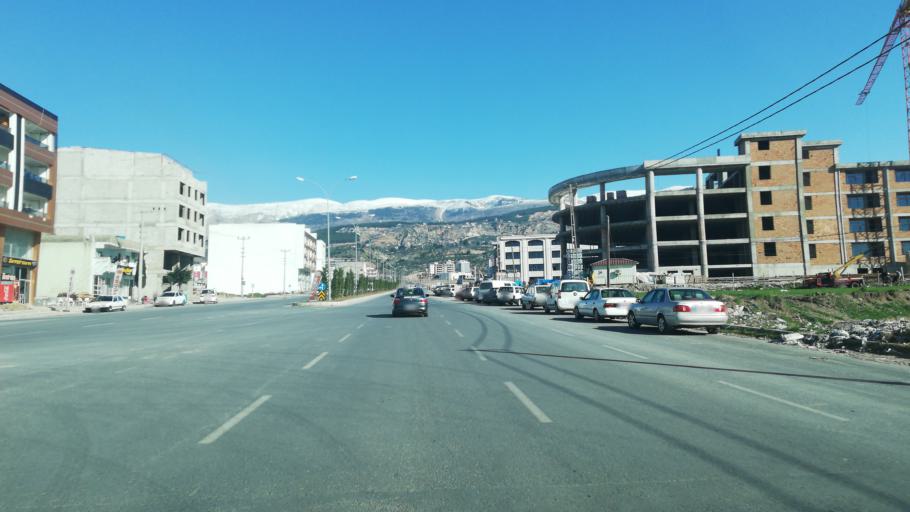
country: TR
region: Kahramanmaras
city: Kahramanmaras
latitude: 37.5746
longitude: 36.9746
